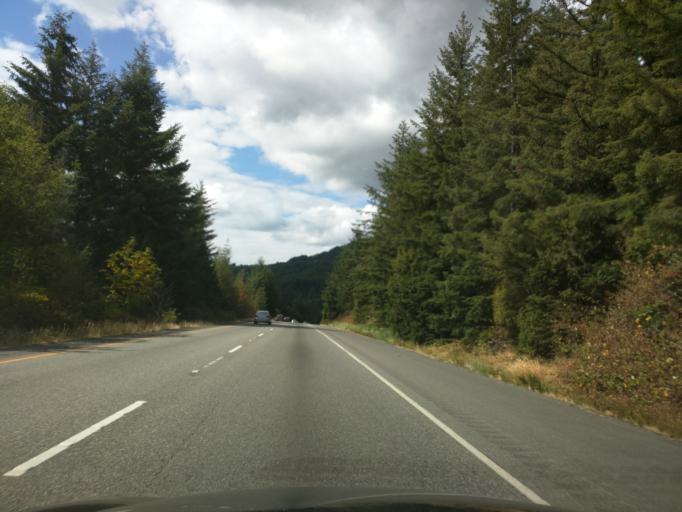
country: US
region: Washington
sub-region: Whatcom County
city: Sudden Valley
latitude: 48.6595
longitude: -122.3701
